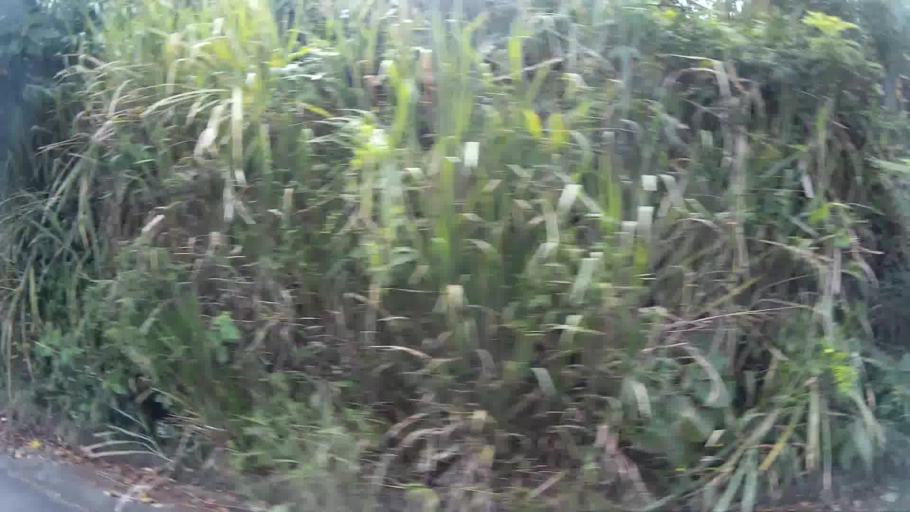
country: CO
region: Risaralda
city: La Virginia
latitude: 4.9398
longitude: -75.8388
